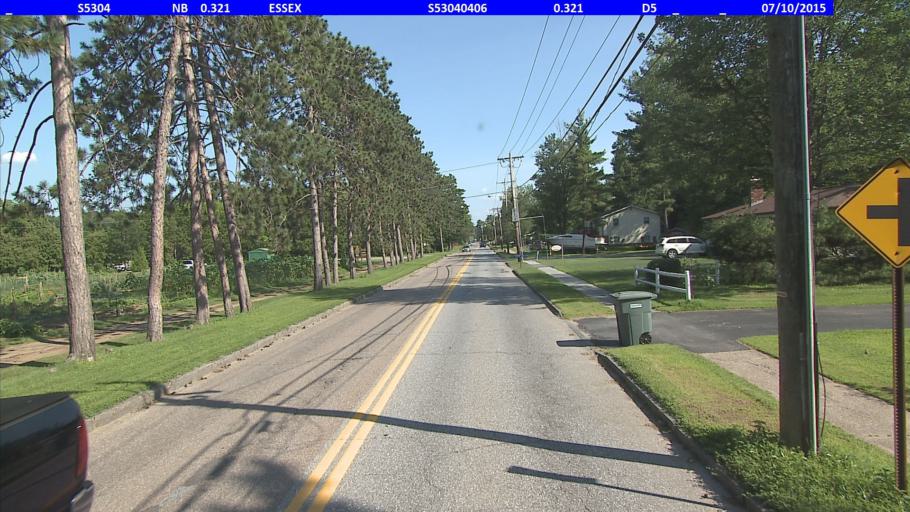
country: US
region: Vermont
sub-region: Chittenden County
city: Essex Junction
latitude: 44.4950
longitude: -73.1289
